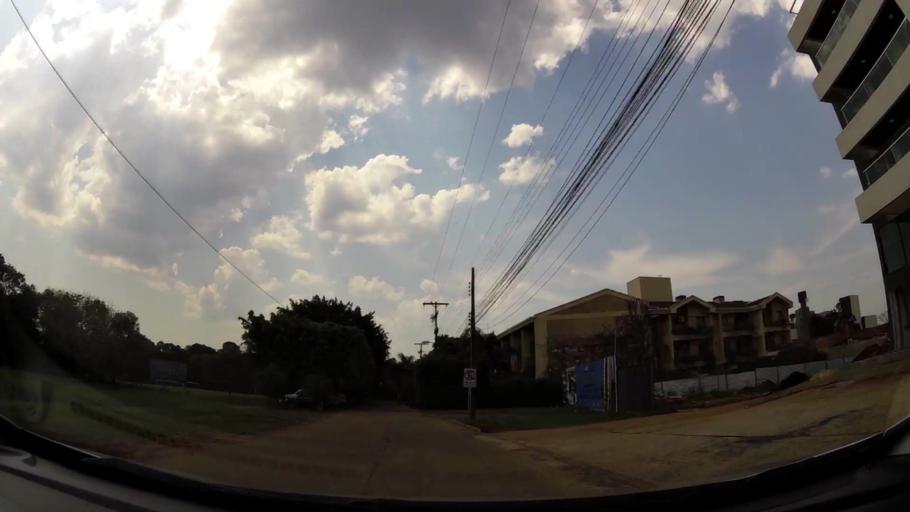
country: PY
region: Alto Parana
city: Ciudad del Este
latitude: -25.4763
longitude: -54.6217
